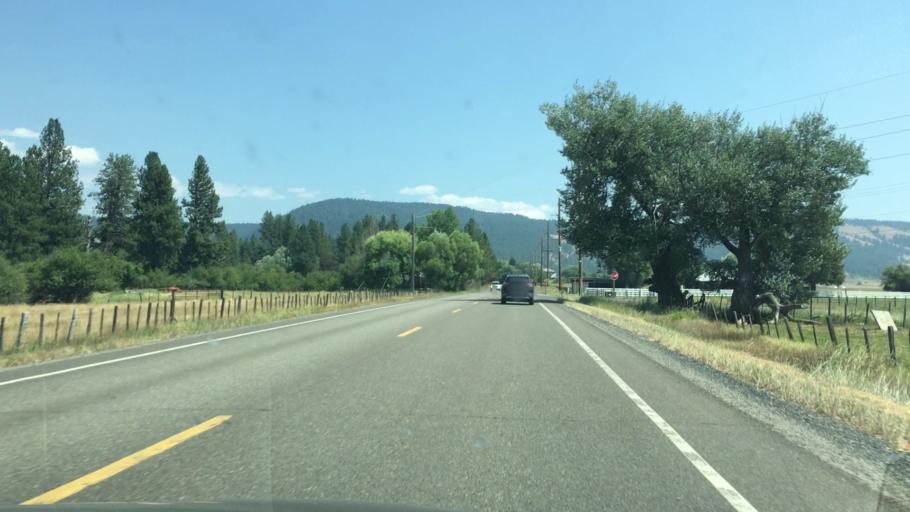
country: US
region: Idaho
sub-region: Valley County
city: McCall
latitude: 44.9635
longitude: -116.2571
